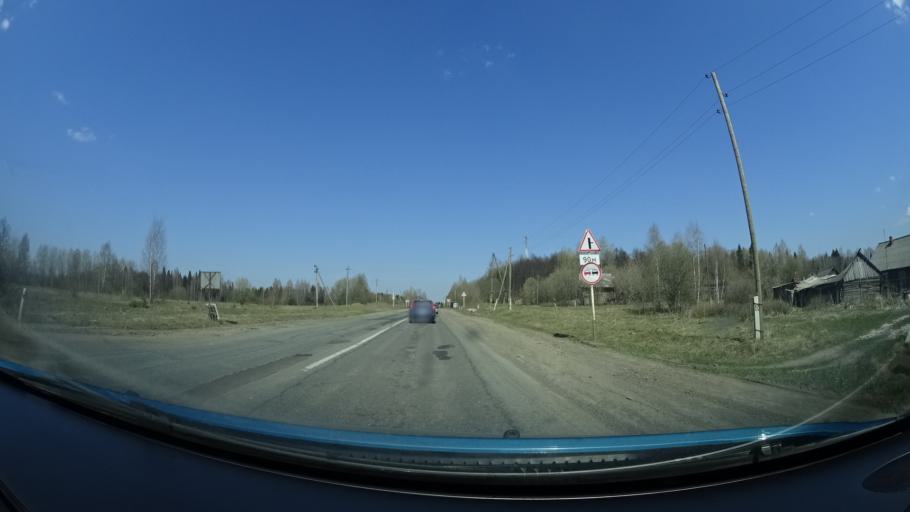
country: RU
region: Perm
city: Kultayevo
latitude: 57.8383
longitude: 55.8224
